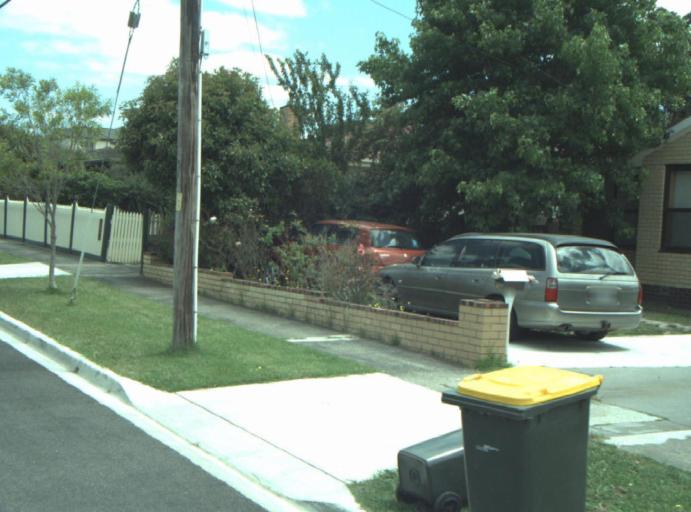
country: AU
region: Victoria
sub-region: Greater Geelong
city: Wandana Heights
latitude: -38.1852
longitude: 144.3284
